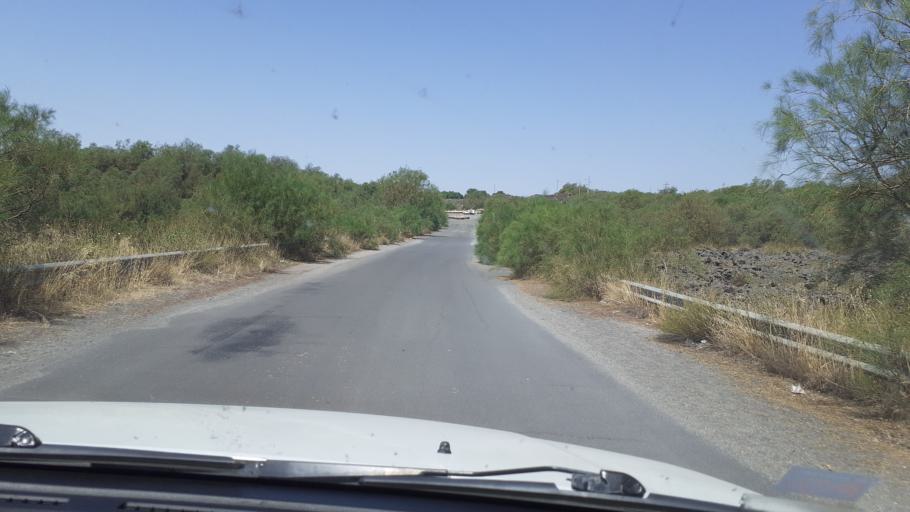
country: IT
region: Sicily
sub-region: Catania
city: Nicolosi
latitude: 37.6450
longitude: 14.9976
